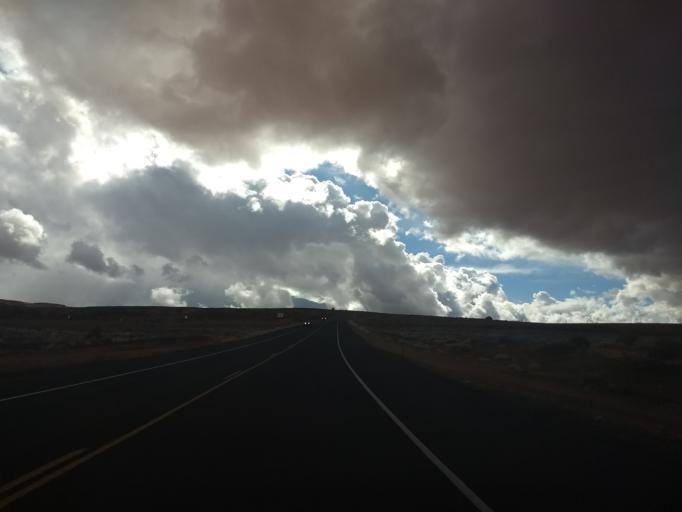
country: US
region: Utah
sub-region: Washington County
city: Washington
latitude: 37.1093
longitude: -113.3944
